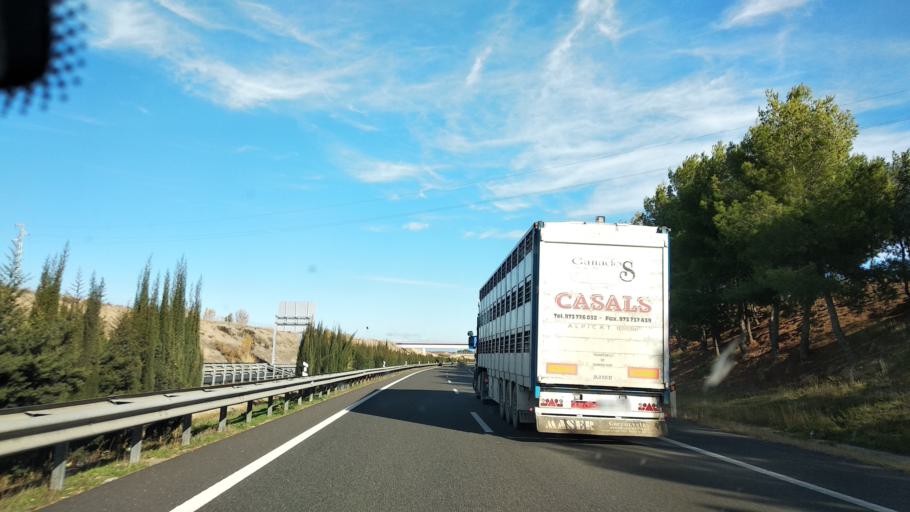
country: ES
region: Catalonia
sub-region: Provincia de Lleida
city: Alpicat
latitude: 41.6538
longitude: 0.5760
